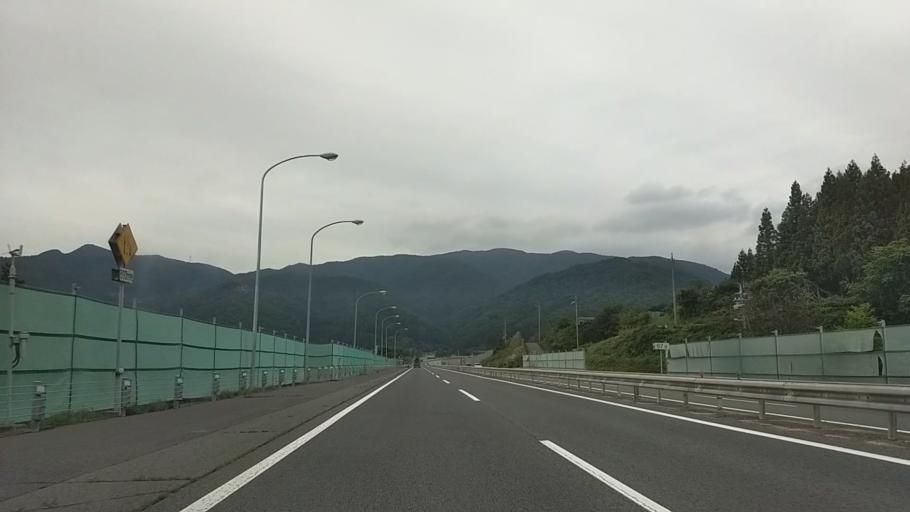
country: JP
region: Nagano
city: Nagano-shi
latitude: 36.5246
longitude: 138.0782
